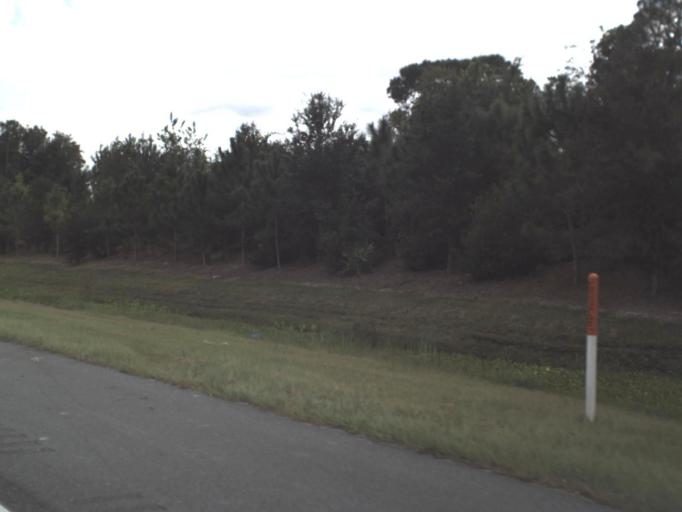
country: US
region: Florida
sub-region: Orange County
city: Winter Garden
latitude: 28.5451
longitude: -81.5850
